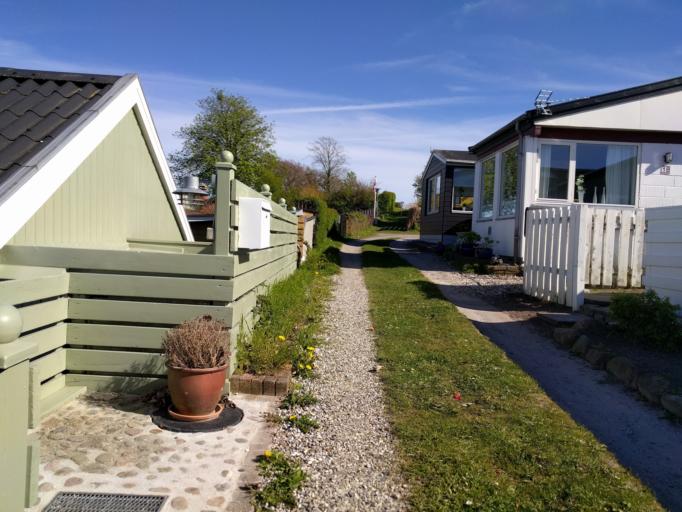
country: DK
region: South Denmark
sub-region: Kerteminde Kommune
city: Munkebo
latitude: 55.4398
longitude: 10.5473
